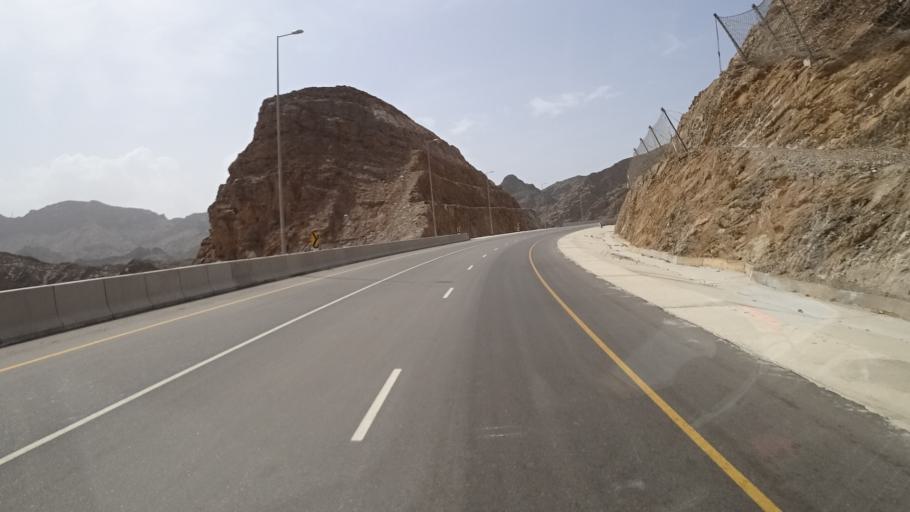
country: OM
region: Muhafazat Masqat
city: Muscat
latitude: 23.4351
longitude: 58.7605
